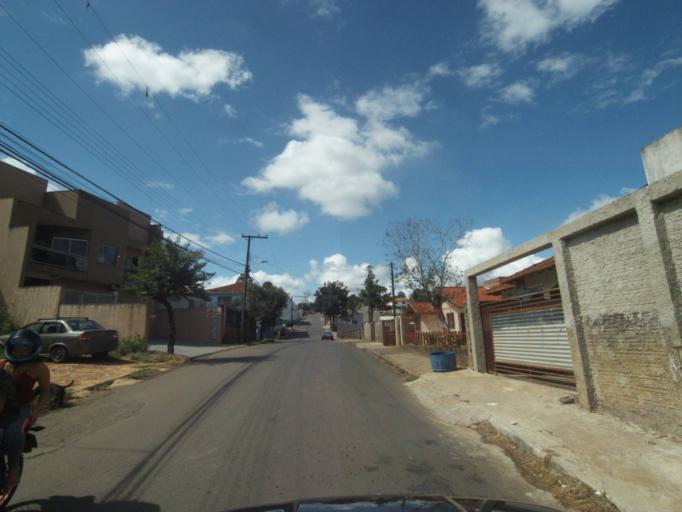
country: BR
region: Parana
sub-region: Telemaco Borba
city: Telemaco Borba
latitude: -24.3192
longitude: -50.6308
